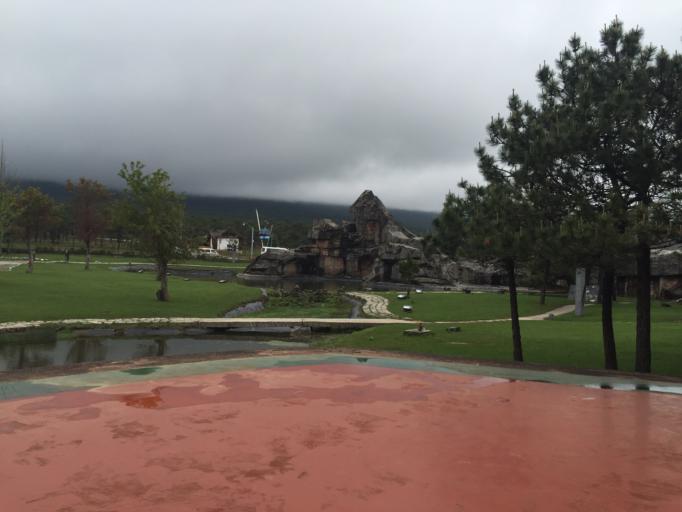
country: CN
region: Yunnan
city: Xiaqiaotou
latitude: 27.1032
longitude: 100.2537
